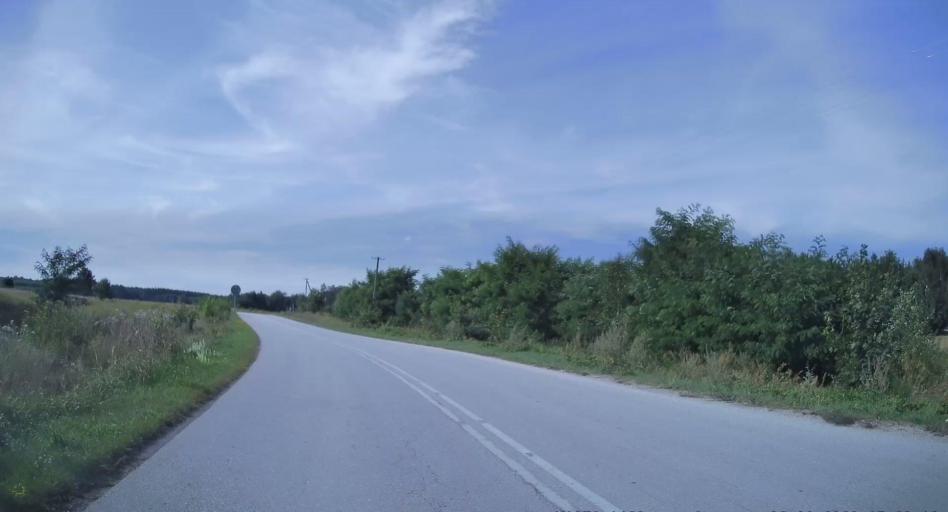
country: PL
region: Lodz Voivodeship
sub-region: Powiat opoczynski
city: Mniszkow
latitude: 51.3518
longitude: 20.0398
